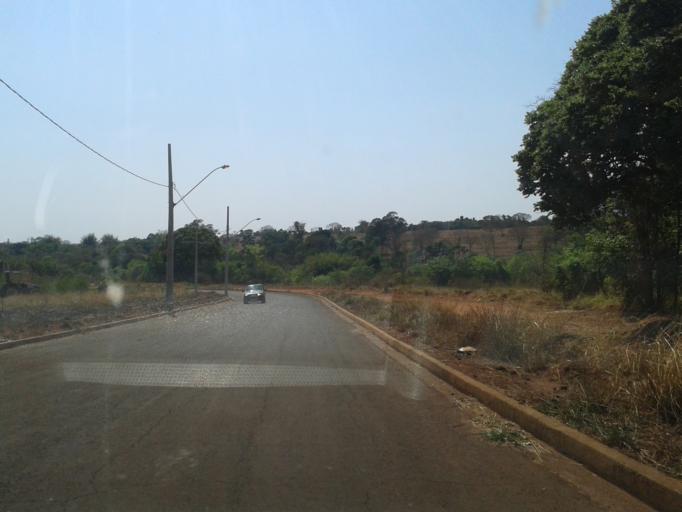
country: BR
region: Minas Gerais
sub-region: Ituiutaba
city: Ituiutaba
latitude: -19.0176
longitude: -49.4494
